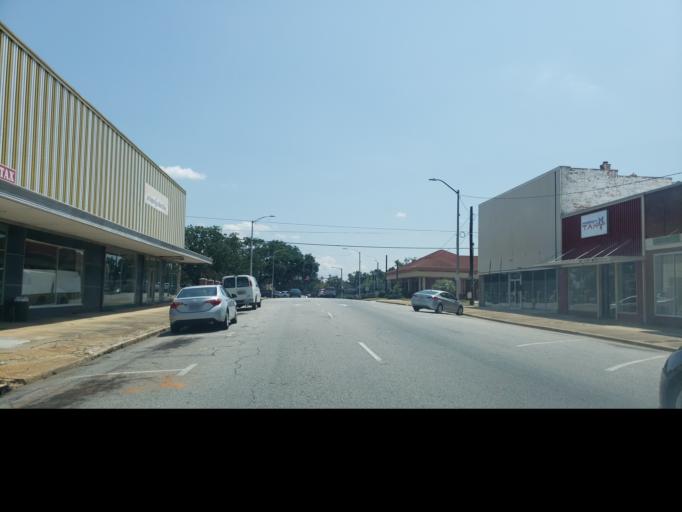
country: US
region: Georgia
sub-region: Dougherty County
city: Albany
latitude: 31.5766
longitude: -84.1536
